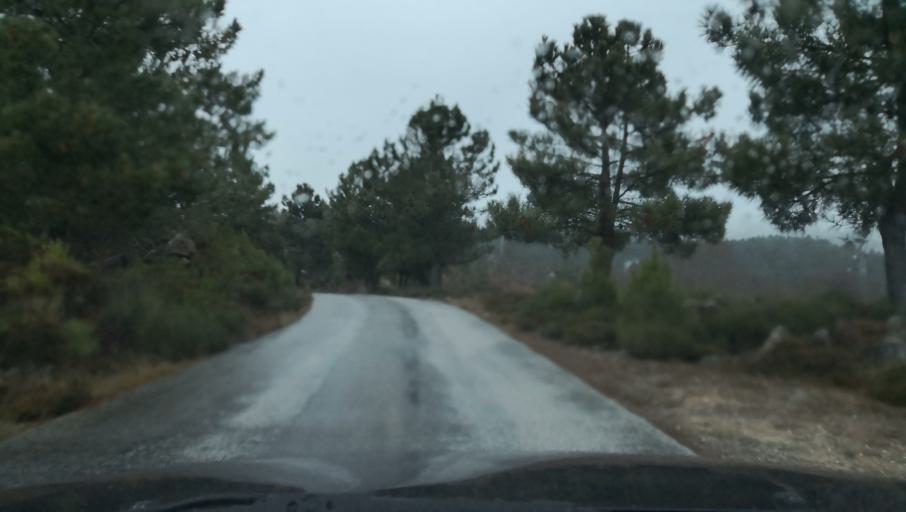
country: PT
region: Vila Real
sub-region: Vila Real
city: Vila Real
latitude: 41.3304
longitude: -7.7861
